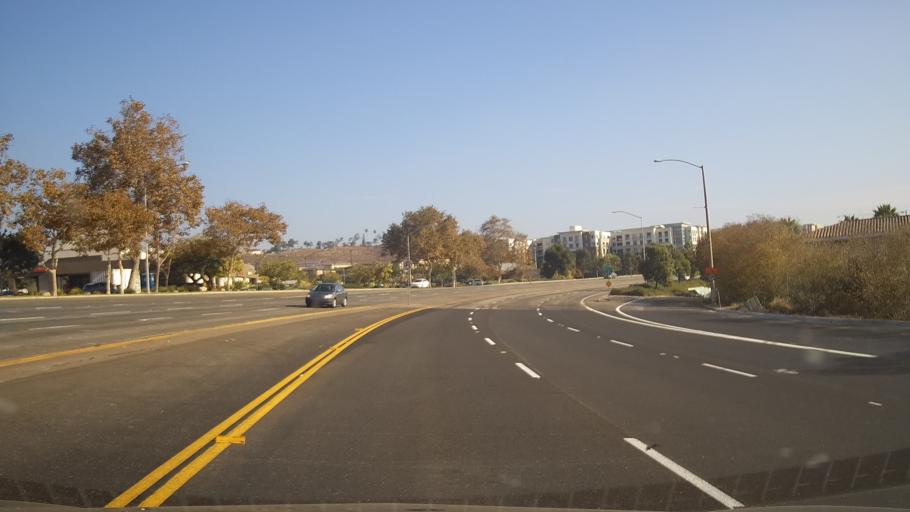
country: US
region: California
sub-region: San Diego County
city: San Diego
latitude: 32.7737
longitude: -117.1564
